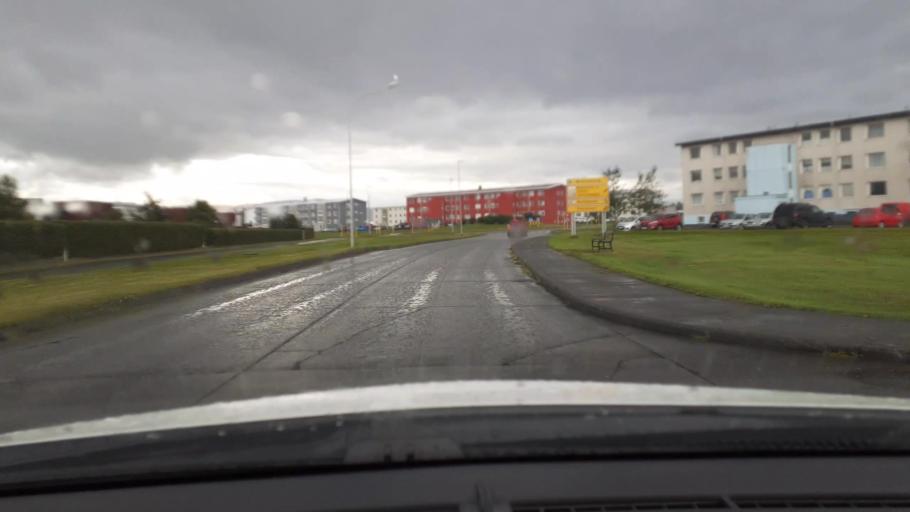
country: IS
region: West
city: Akranes
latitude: 64.3221
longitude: -22.0613
